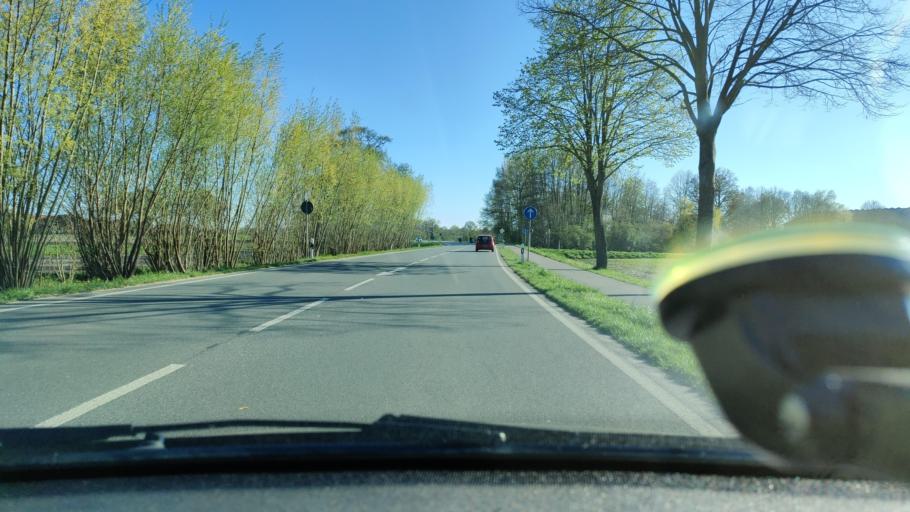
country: DE
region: North Rhine-Westphalia
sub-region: Regierungsbezirk Munster
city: Legden
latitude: 51.9988
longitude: 7.1285
